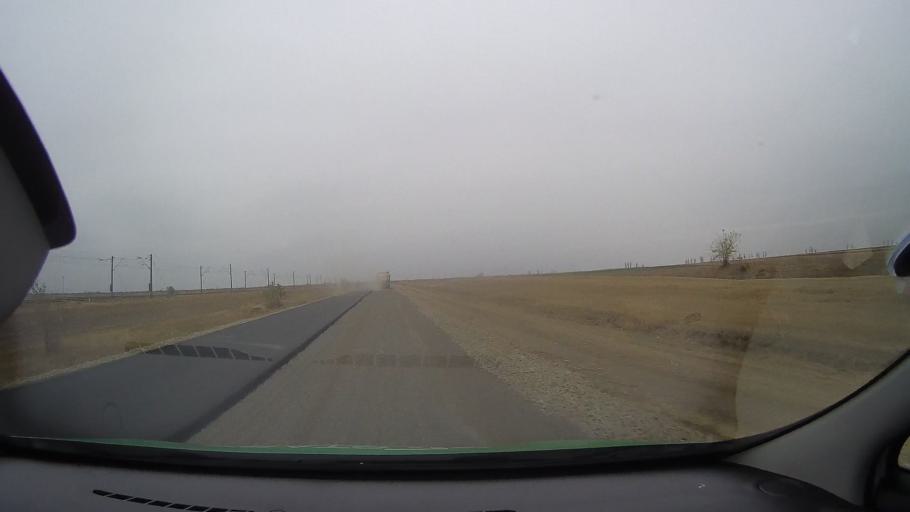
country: RO
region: Braila
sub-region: Comuna Baraganul
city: Baraganul
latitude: 44.7947
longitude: 27.5323
